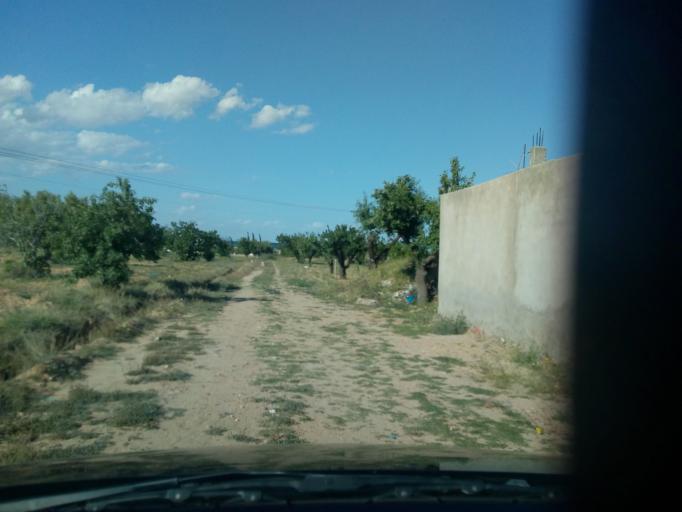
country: TN
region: Safaqis
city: Sfax
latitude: 34.7299
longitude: 10.6130
